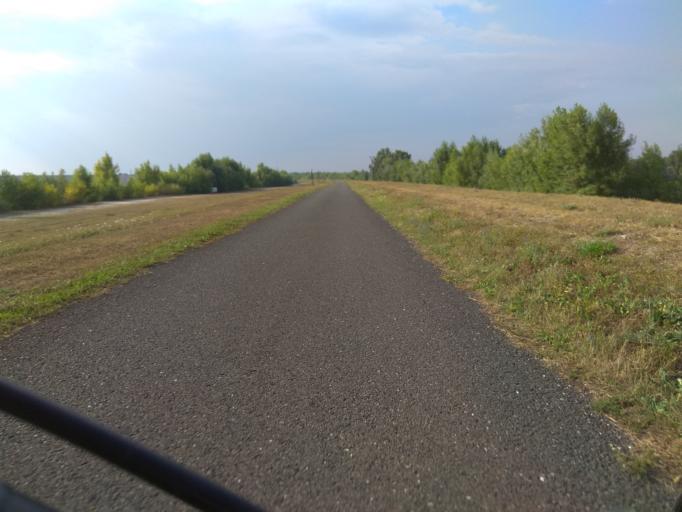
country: SK
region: Trnavsky
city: Gabcikovo
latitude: 47.8702
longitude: 17.5559
